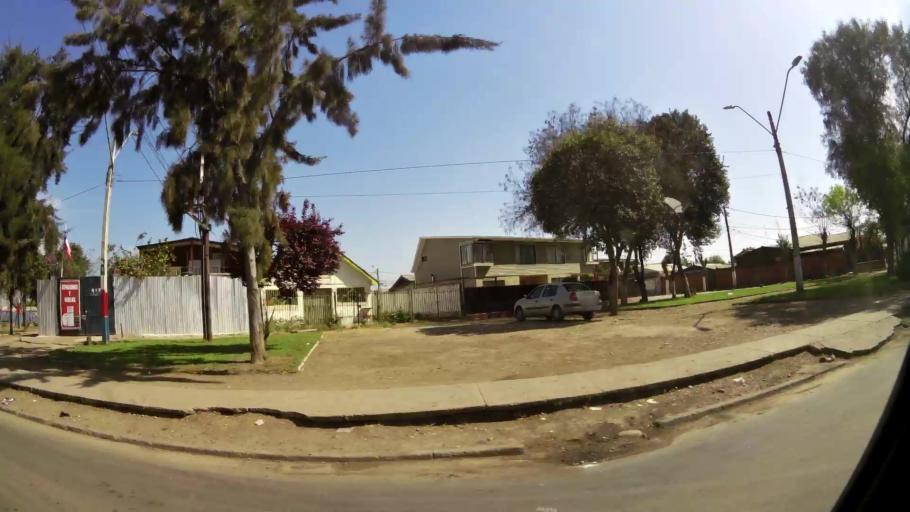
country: CL
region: Santiago Metropolitan
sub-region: Provincia de Santiago
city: Lo Prado
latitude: -33.4747
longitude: -70.7084
